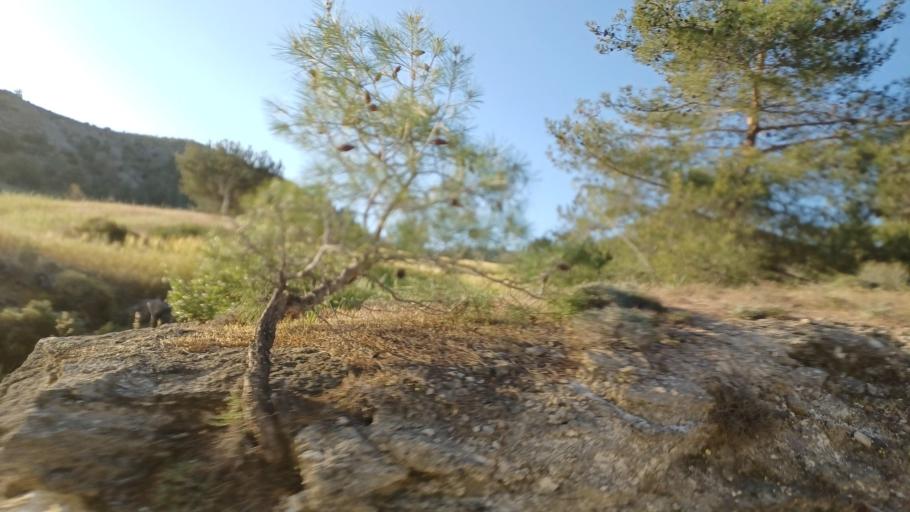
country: CY
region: Lefkosia
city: Peristerona
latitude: 35.0658
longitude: 33.0437
